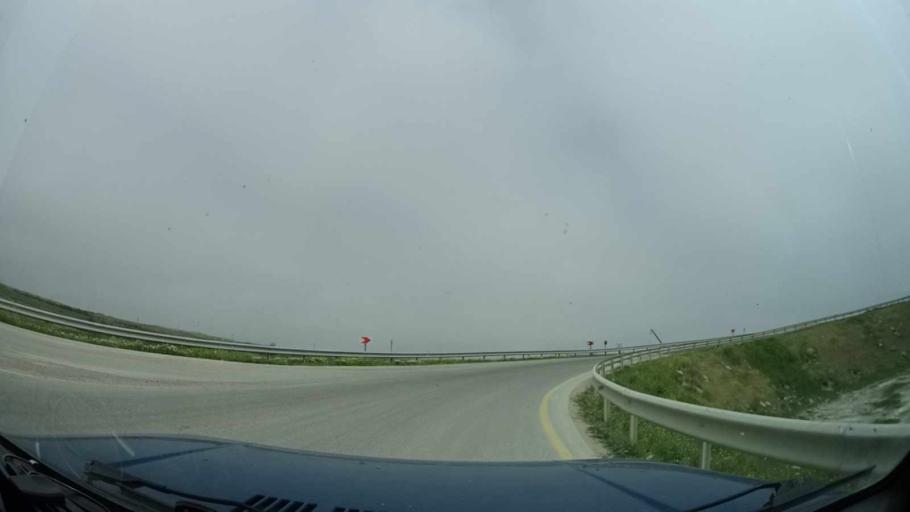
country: AZ
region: Xizi
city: Kilyazi
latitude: 40.8704
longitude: 49.3539
